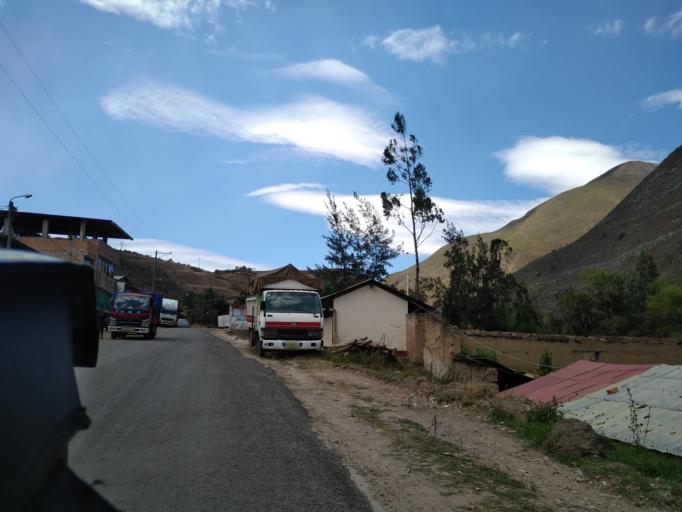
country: PE
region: Amazonas
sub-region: Provincia de Chachapoyas
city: Duraznopampa
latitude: -6.5694
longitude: -77.8276
